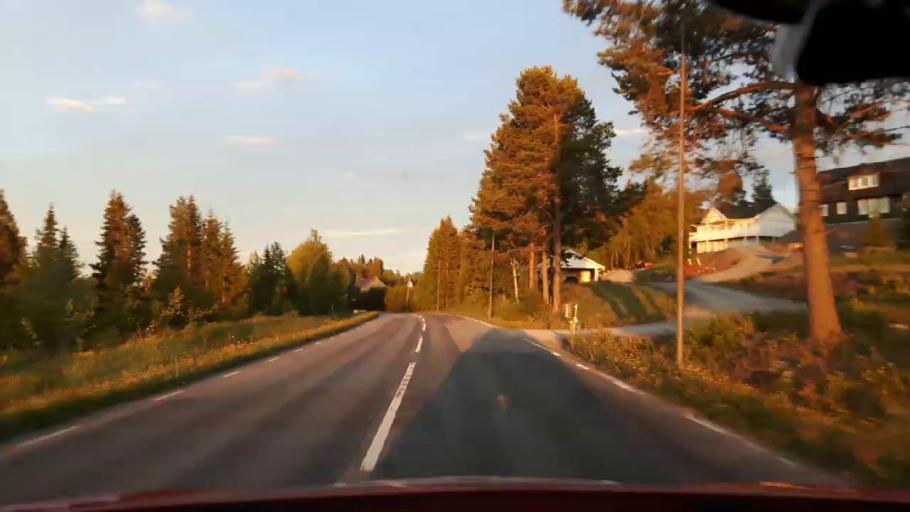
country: SE
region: Jaemtland
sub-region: OEstersunds Kommun
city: Ostersund
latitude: 63.1378
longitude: 14.6327
